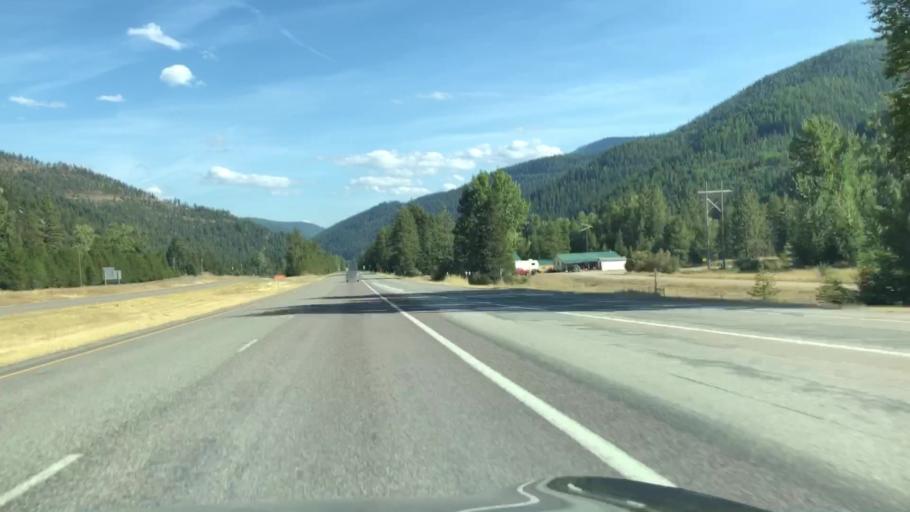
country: US
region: Montana
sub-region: Sanders County
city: Thompson Falls
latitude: 47.3743
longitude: -115.3469
